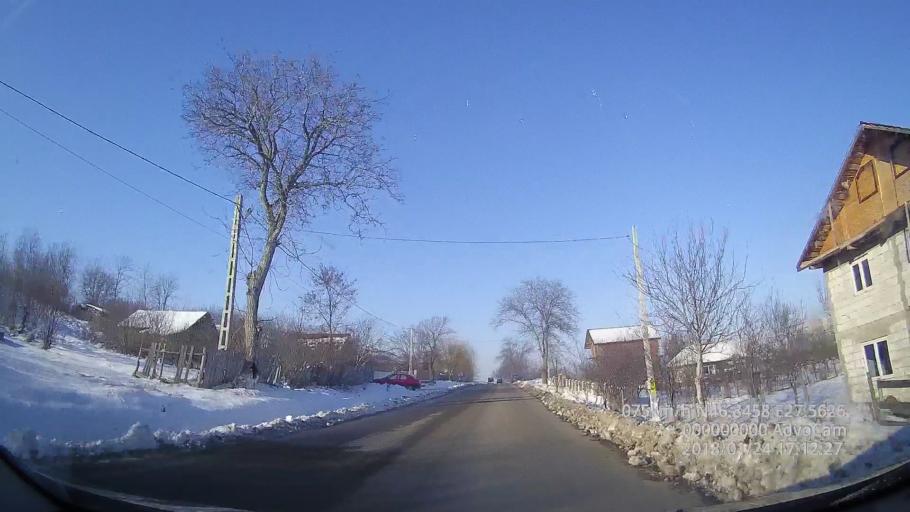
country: RO
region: Vaslui
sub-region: Comuna Rebricea
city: Rebricea
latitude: 46.8466
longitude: 27.5626
